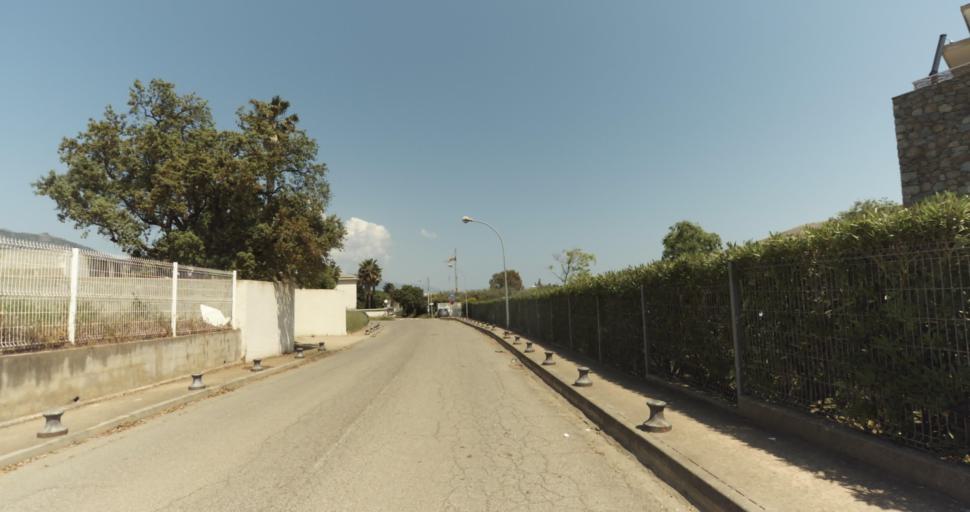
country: FR
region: Corsica
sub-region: Departement de la Haute-Corse
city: Biguglia
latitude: 42.5931
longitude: 9.4347
